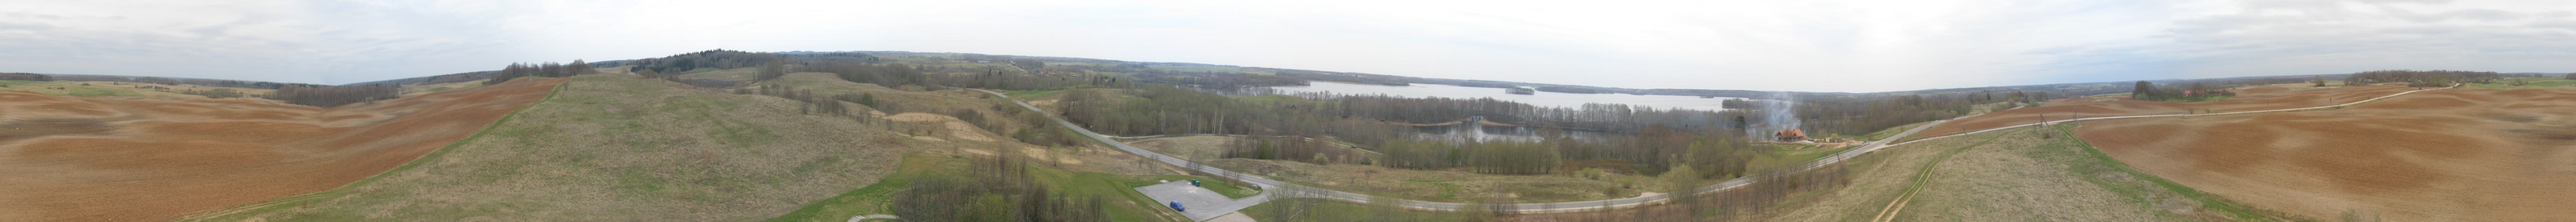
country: LT
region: Utenos apskritis
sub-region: Anyksciai
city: Anyksciai
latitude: 55.4832
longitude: 25.2787
